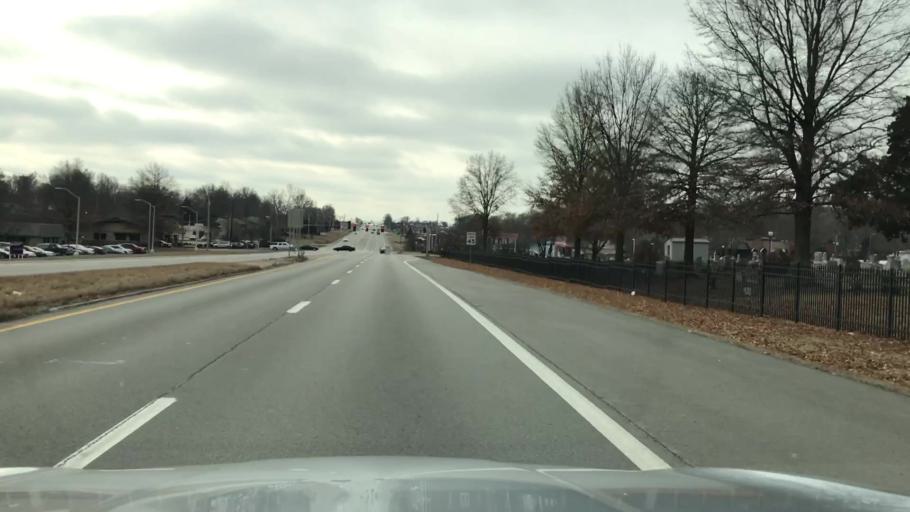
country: US
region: Missouri
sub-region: Jackson County
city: Lees Summit
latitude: 38.9166
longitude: -94.3622
